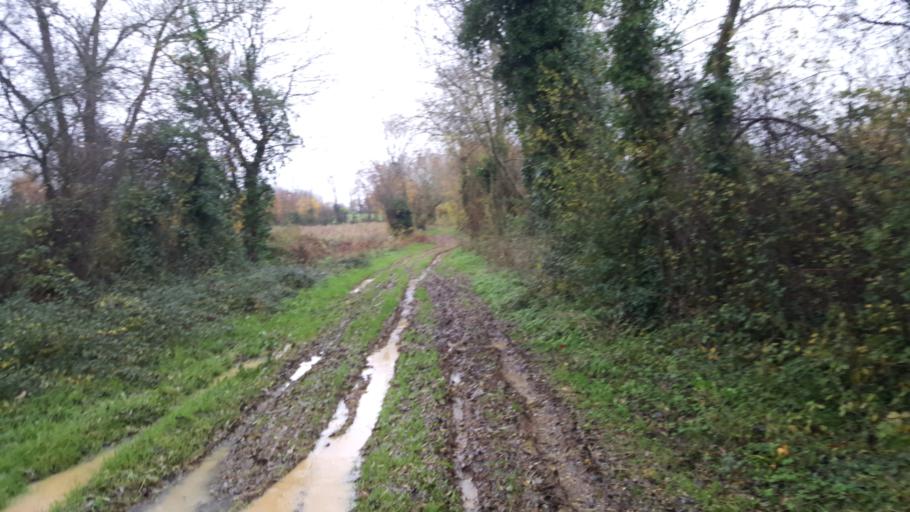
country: FR
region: Poitou-Charentes
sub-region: Departement des Deux-Sevres
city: Melle
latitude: 46.2296
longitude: -0.1286
